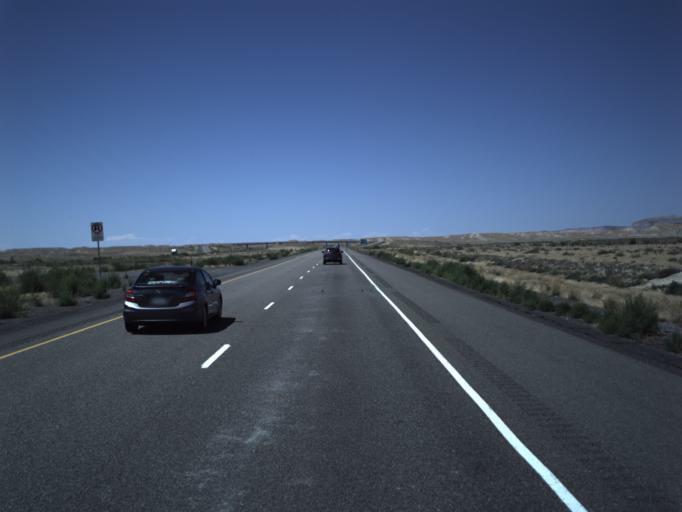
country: US
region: Utah
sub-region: Grand County
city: Moab
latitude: 38.9428
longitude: -109.6010
